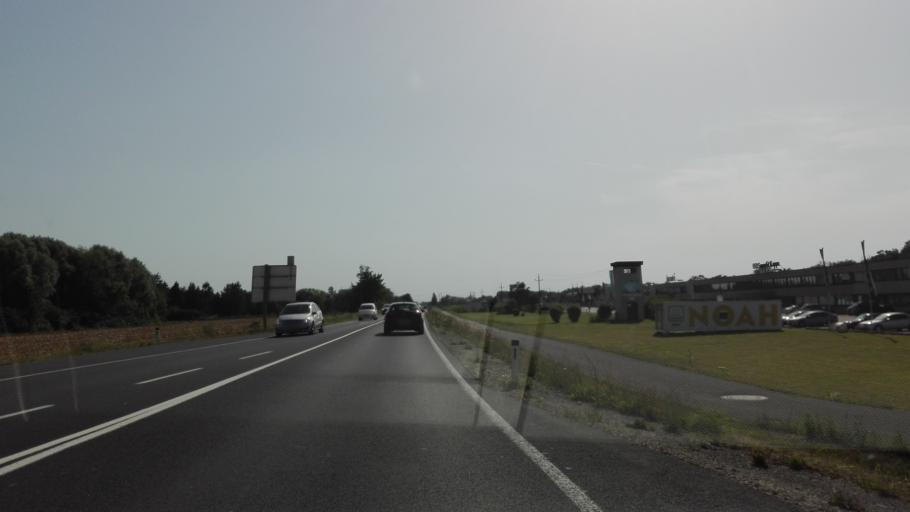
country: AT
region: Upper Austria
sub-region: Politischer Bezirk Linz-Land
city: Horsching
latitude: 48.2129
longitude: 14.1789
